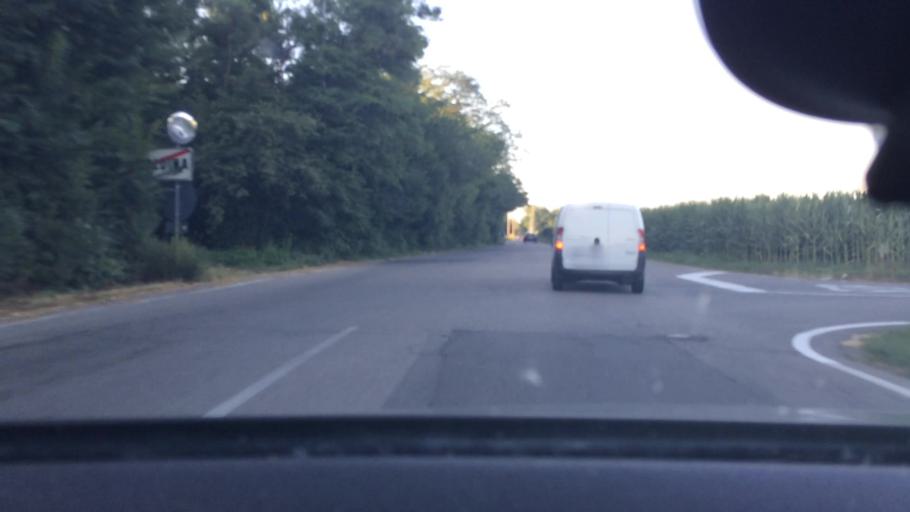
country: IT
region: Lombardy
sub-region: Citta metropolitana di Milano
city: Rescaldina
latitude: 45.6263
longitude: 8.9629
